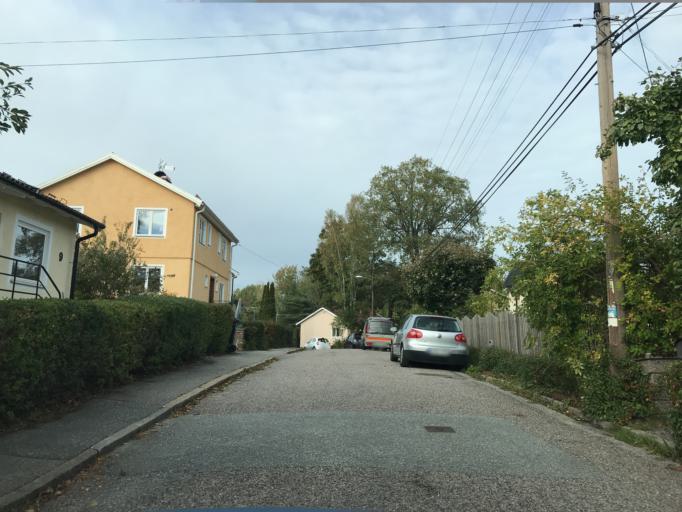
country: SE
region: Stockholm
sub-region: Huddinge Kommun
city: Huddinge
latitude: 59.2755
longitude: 17.9766
